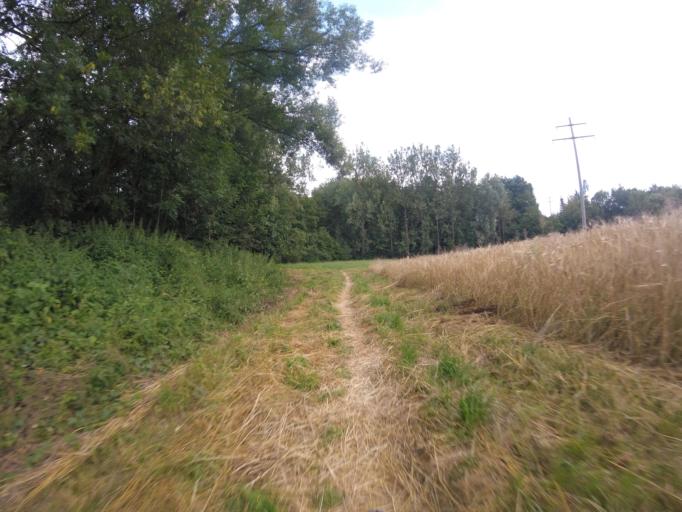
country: DE
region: Baden-Wuerttemberg
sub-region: Regierungsbezirk Stuttgart
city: Oppenweiler
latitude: 48.9636
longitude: 9.4648
